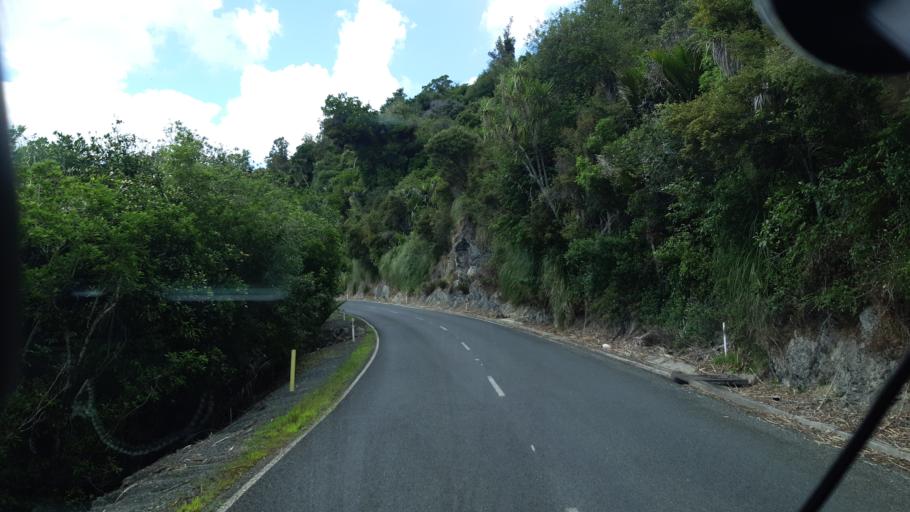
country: NZ
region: Northland
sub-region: Far North District
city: Taipa
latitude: -35.2486
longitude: 173.5306
